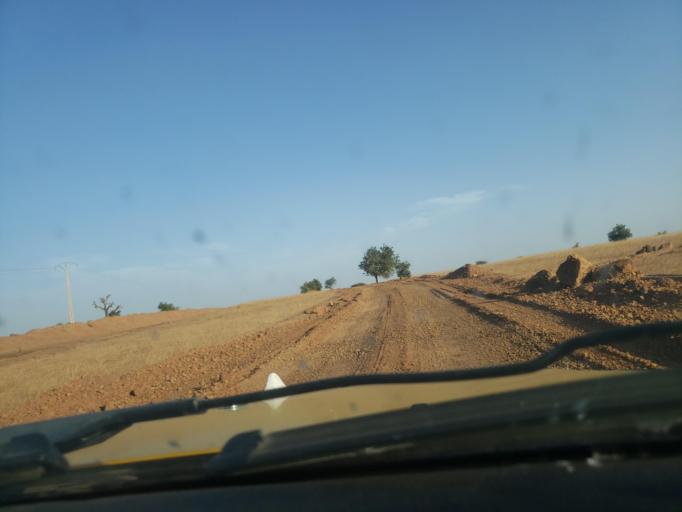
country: SN
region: Louga
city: Dara
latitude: 15.4272
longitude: -15.7426
